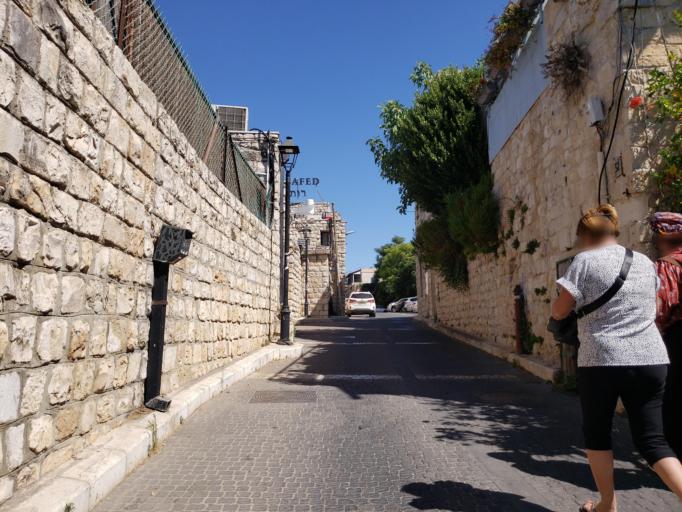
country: IL
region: Northern District
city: Safed
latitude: 32.9633
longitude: 35.4945
